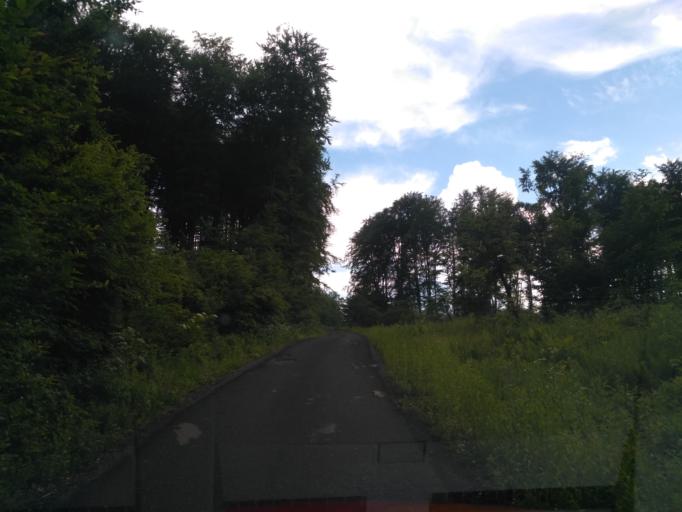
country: SK
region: Presovsky
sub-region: Okres Presov
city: Presov
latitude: 48.9639
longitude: 21.1738
